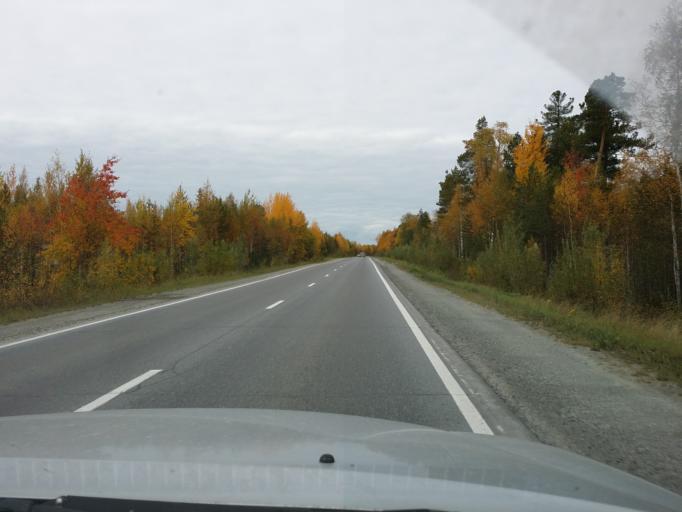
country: RU
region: Khanty-Mansiyskiy Avtonomnyy Okrug
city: Megion
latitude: 61.1275
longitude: 75.8022
